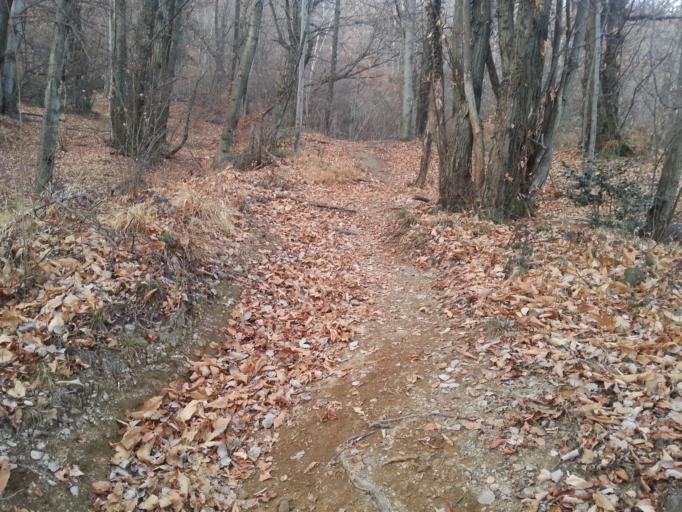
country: CH
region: Ticino
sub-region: Lugano District
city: Pura
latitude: 46.0273
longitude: 8.8513
